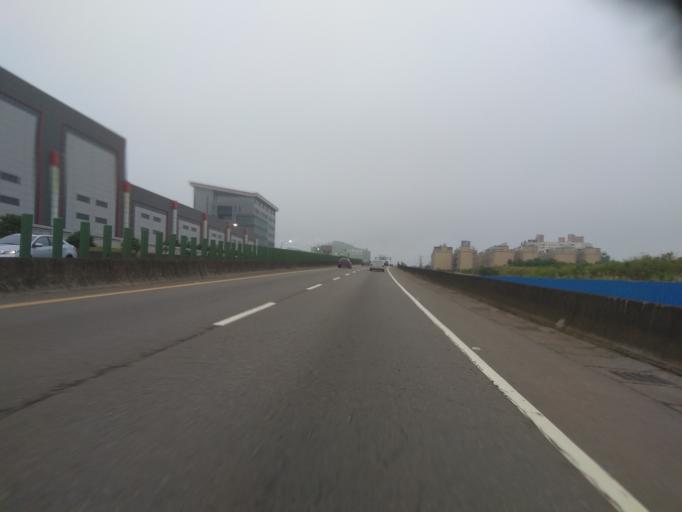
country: TW
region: Taiwan
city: Taoyuan City
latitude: 24.9524
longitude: 121.1585
